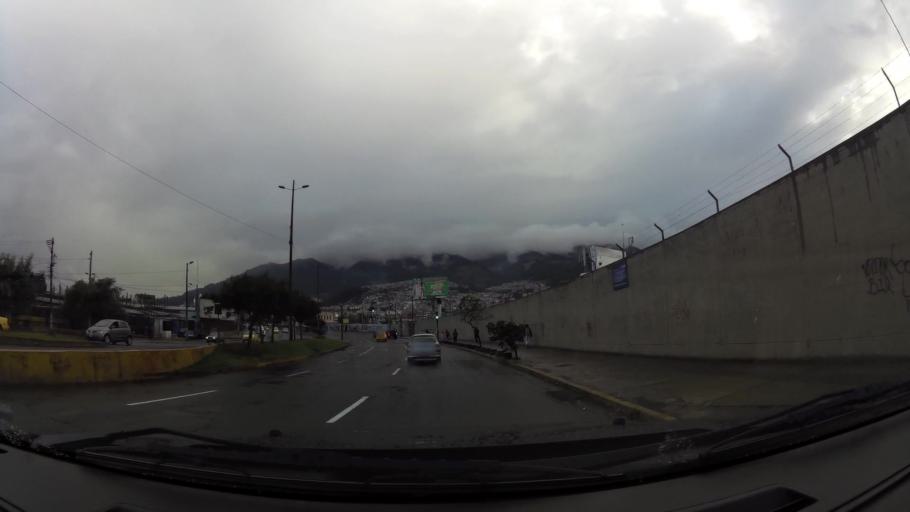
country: EC
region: Pichincha
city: Quito
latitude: -0.1087
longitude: -78.4884
